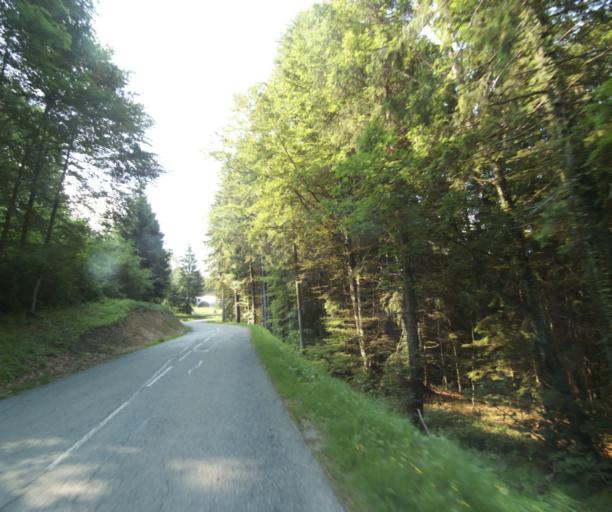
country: FR
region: Rhone-Alpes
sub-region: Departement de la Haute-Savoie
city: Lyaud
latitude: 46.2984
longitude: 6.5094
